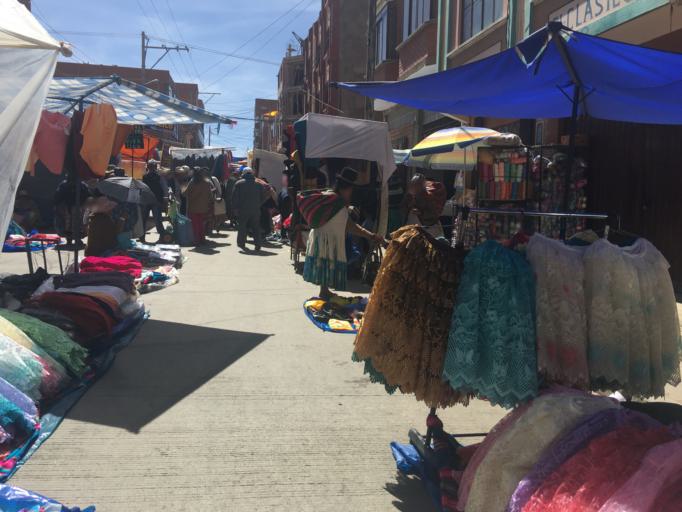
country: BO
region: La Paz
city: La Paz
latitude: -16.4923
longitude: -68.1711
